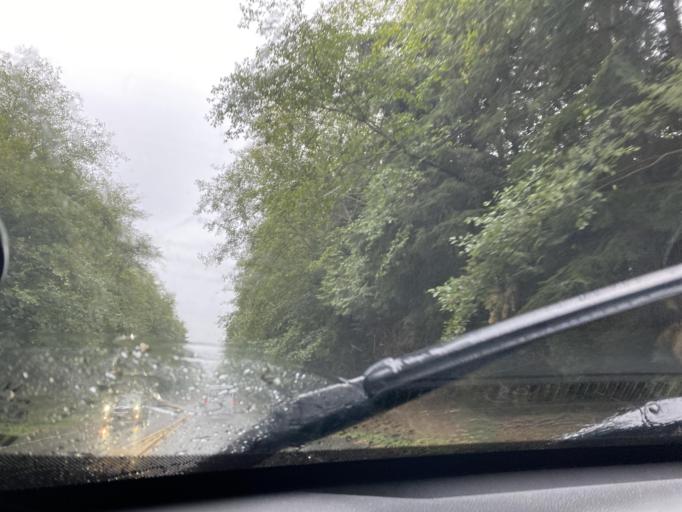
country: US
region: Washington
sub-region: Kitsap County
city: Bainbridge Island
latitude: 47.6710
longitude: -122.5313
